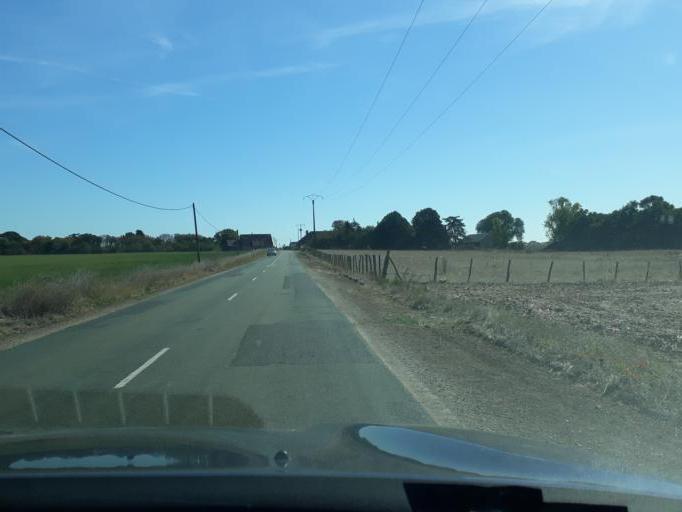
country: FR
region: Centre
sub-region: Departement du Loir-et-Cher
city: Ouzouer-le-Marche
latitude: 47.9298
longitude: 1.5182
